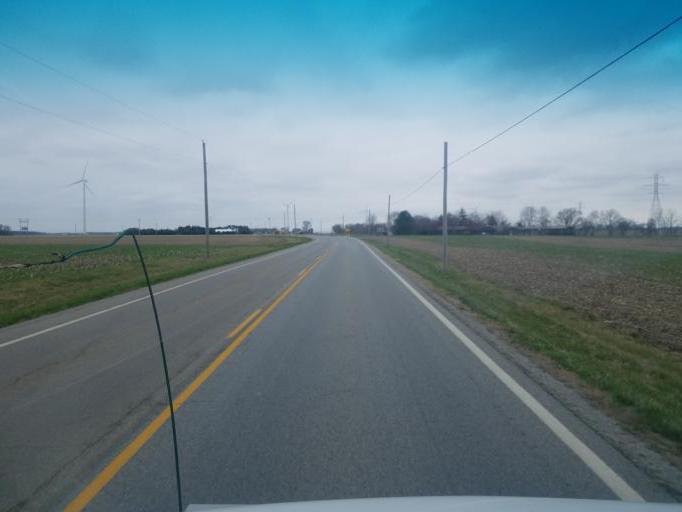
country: US
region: Ohio
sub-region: Van Wert County
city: Van Wert
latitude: 40.9274
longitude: -84.5305
